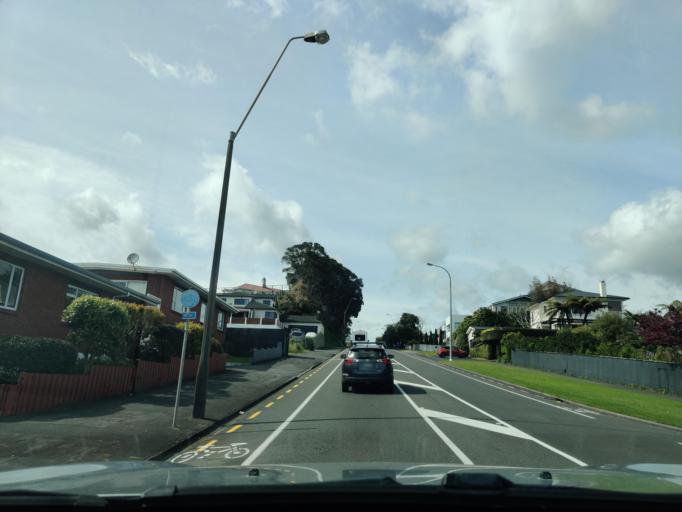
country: NZ
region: Taranaki
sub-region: New Plymouth District
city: New Plymouth
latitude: -39.0585
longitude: 174.0845
